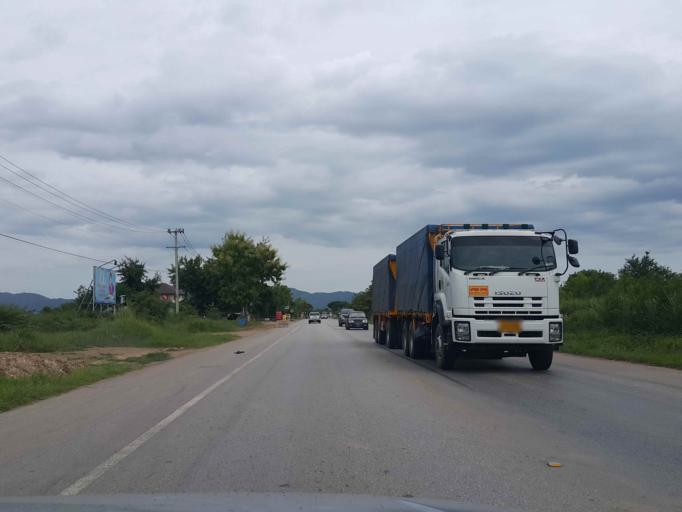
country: TH
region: Lampang
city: Lampang
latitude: 18.2610
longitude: 99.4720
